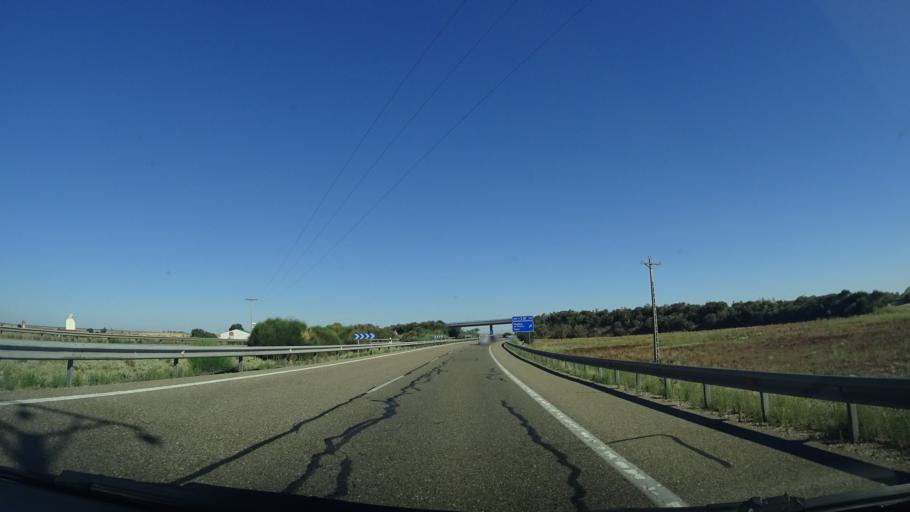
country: ES
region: Castille and Leon
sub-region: Provincia de Valladolid
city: Villardefrades
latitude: 41.7186
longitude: -5.2467
